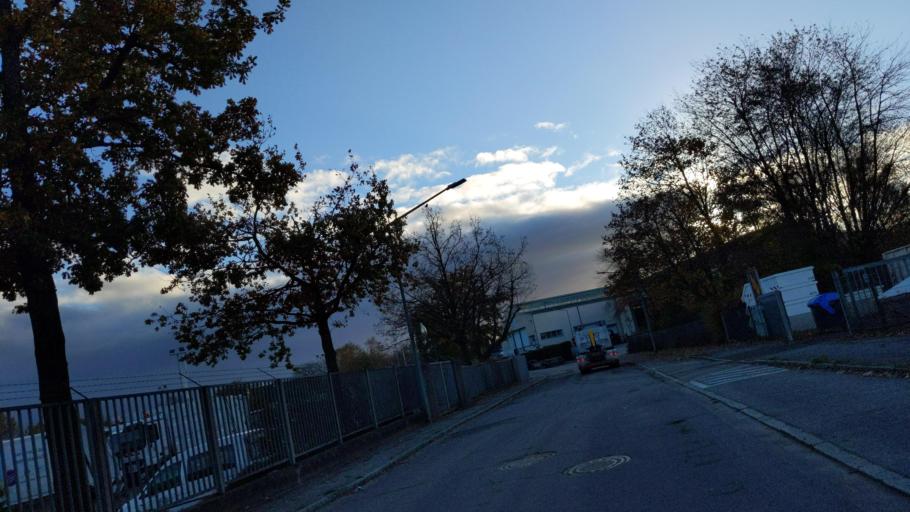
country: DE
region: Schleswig-Holstein
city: Neustadt in Holstein
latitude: 54.0955
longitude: 10.7919
